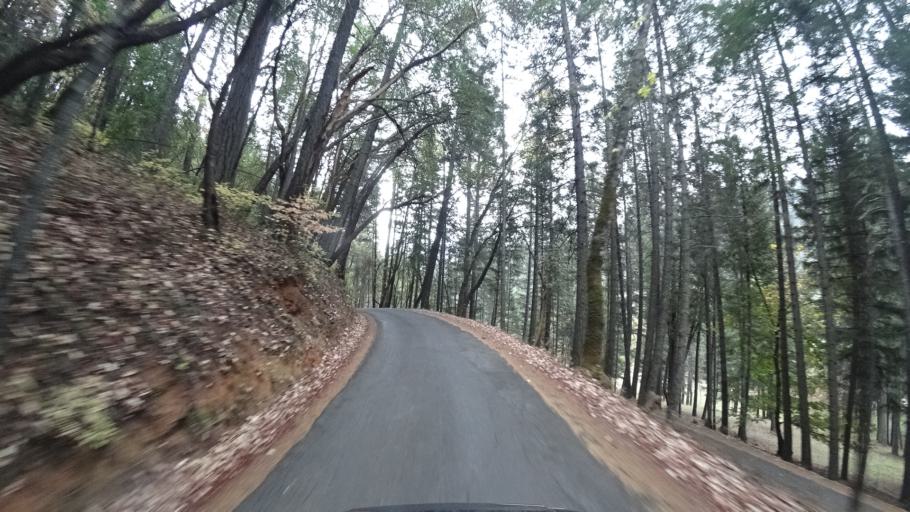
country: US
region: California
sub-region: Siskiyou County
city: Happy Camp
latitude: 41.7968
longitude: -123.3434
